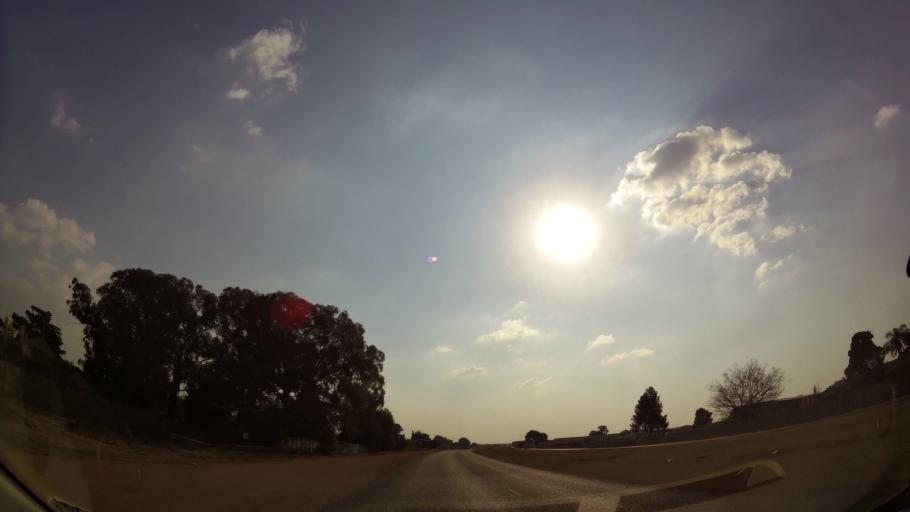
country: ZA
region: Gauteng
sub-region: Ekurhuleni Metropolitan Municipality
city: Benoni
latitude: -26.1160
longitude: 28.2695
